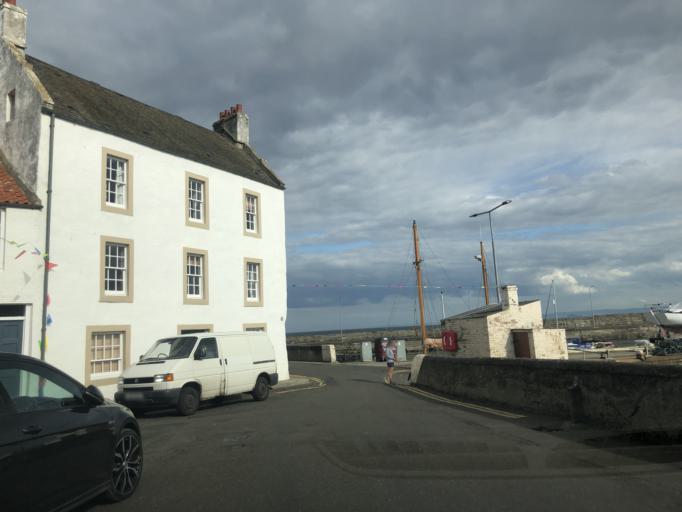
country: GB
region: Scotland
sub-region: Fife
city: Saint Monance
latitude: 56.2050
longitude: -2.7652
